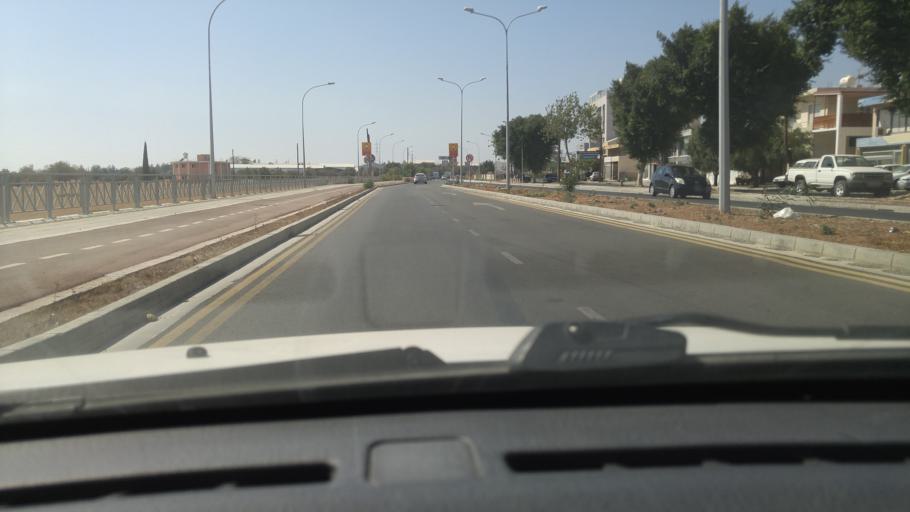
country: CY
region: Limassol
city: Pano Polemidia
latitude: 34.6810
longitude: 32.9882
